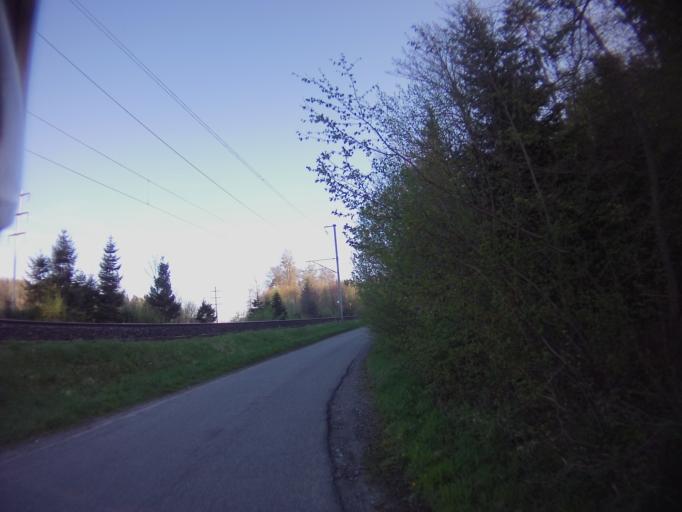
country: CH
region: Zurich
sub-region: Bezirk Affoltern
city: Obfelden / Toussen
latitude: 47.2668
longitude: 8.4408
